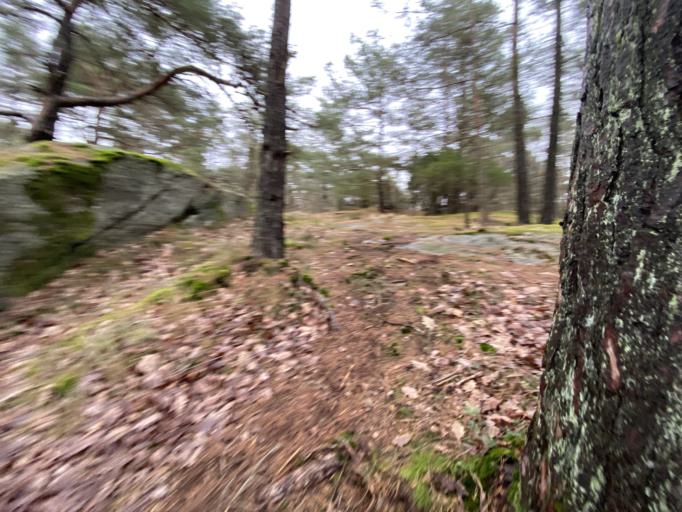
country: SE
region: Vaestra Goetaland
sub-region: Molndal
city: Moelndal
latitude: 57.7105
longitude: 12.0350
